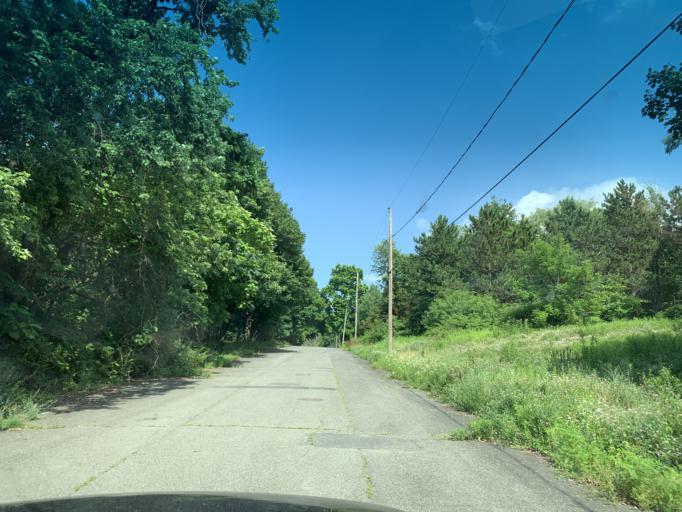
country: US
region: Pennsylvania
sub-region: Schuylkill County
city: Ashland
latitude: 40.8022
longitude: -76.3393
